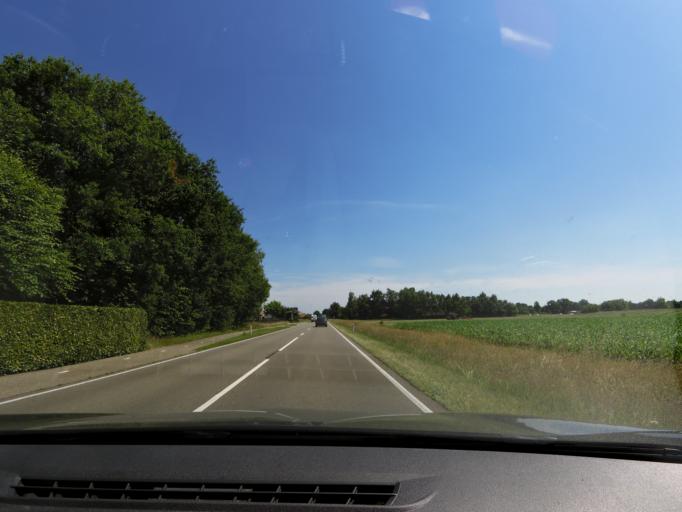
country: NL
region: Gelderland
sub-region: Berkelland
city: Eibergen
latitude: 52.1176
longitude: 6.6366
